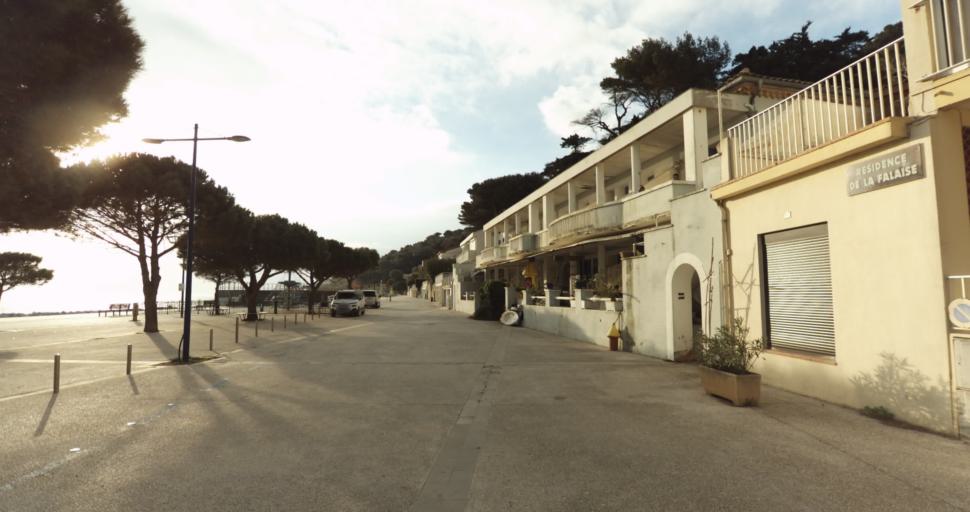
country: FR
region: Languedoc-Roussillon
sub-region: Departement de l'Aude
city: Leucate
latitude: 42.9305
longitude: 3.0388
